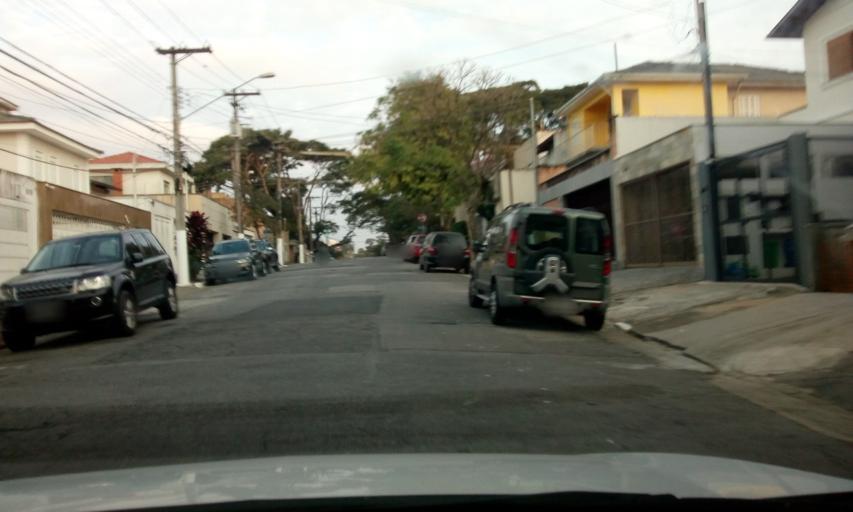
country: BR
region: Sao Paulo
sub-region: Sao Paulo
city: Sao Paulo
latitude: -23.6129
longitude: -46.6469
